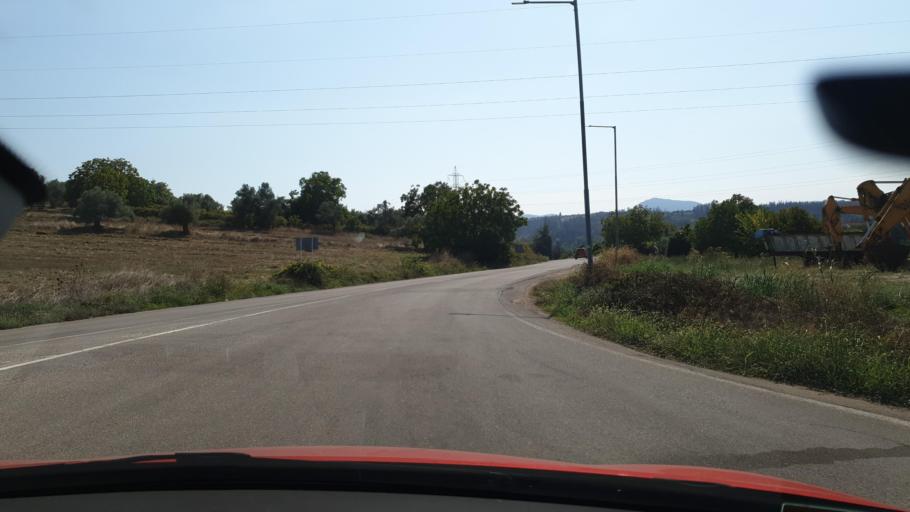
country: GR
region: Central Greece
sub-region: Nomos Evvoias
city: Mantoudi
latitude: 38.8211
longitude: 23.4157
